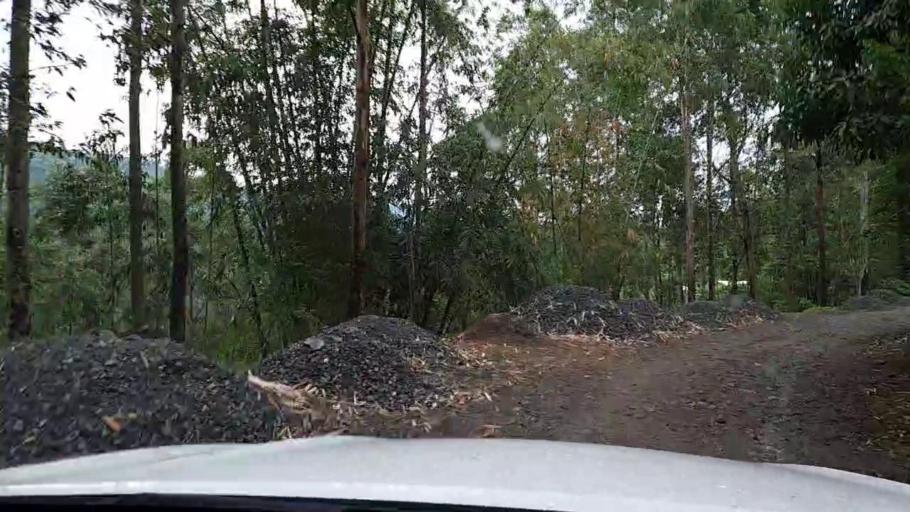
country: RW
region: Western Province
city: Cyangugu
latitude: -2.5441
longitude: 29.0374
